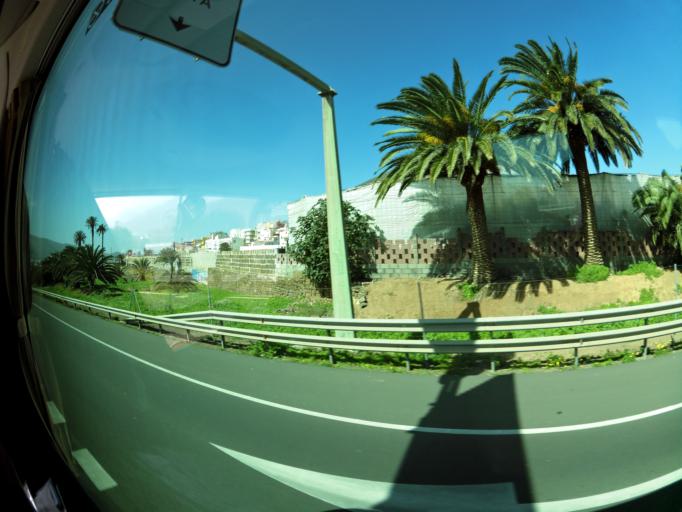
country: ES
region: Canary Islands
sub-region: Provincia de Las Palmas
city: Guia
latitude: 28.1451
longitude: -15.6347
